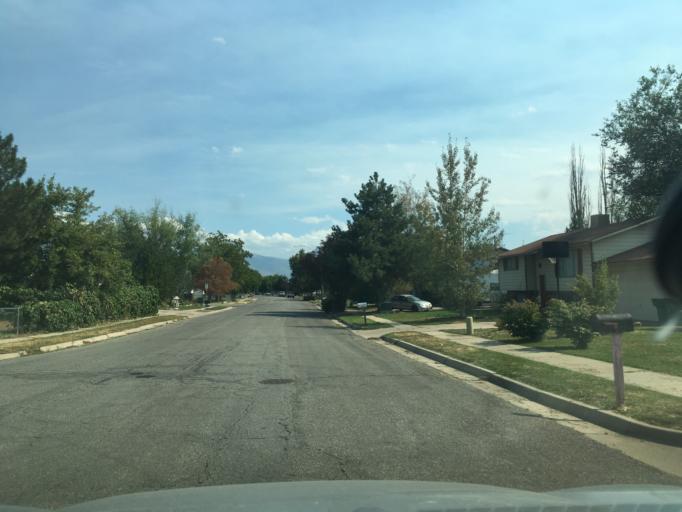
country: US
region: Utah
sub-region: Davis County
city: Clearfield
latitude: 41.0830
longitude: -112.0038
